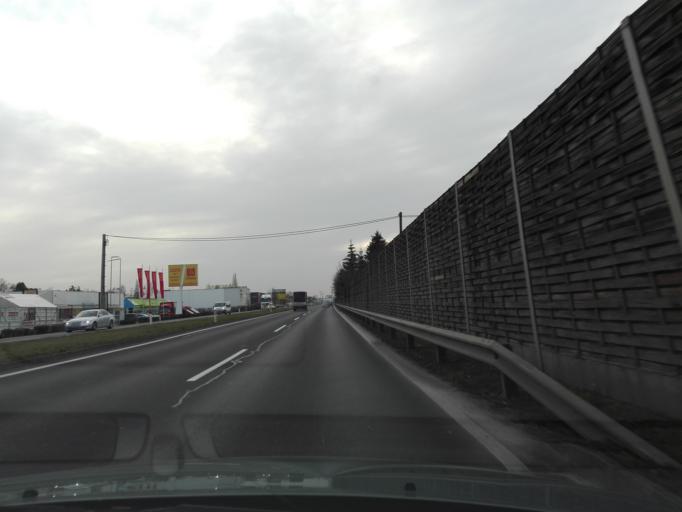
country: AT
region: Upper Austria
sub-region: Politischer Bezirk Linz-Land
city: Traun
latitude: 48.2384
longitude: 14.2435
